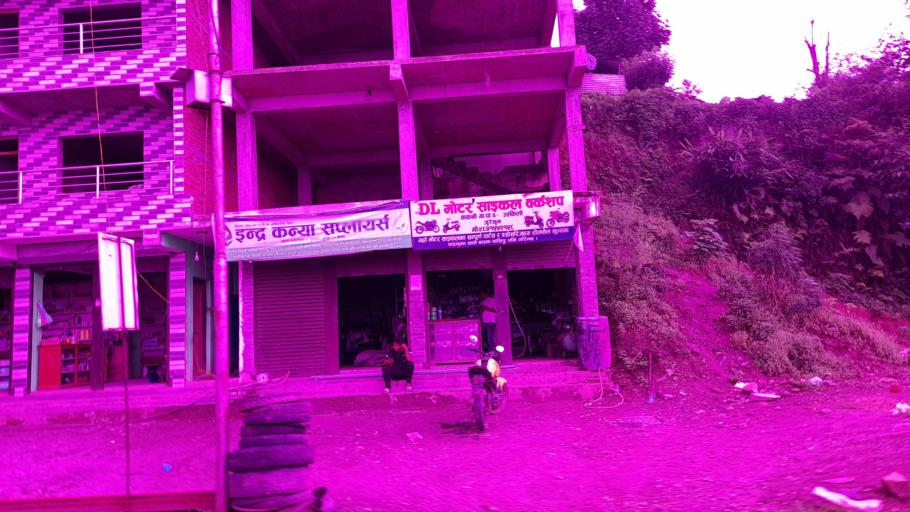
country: NP
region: Central Region
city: Kirtipur
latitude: 27.8292
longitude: 85.2096
